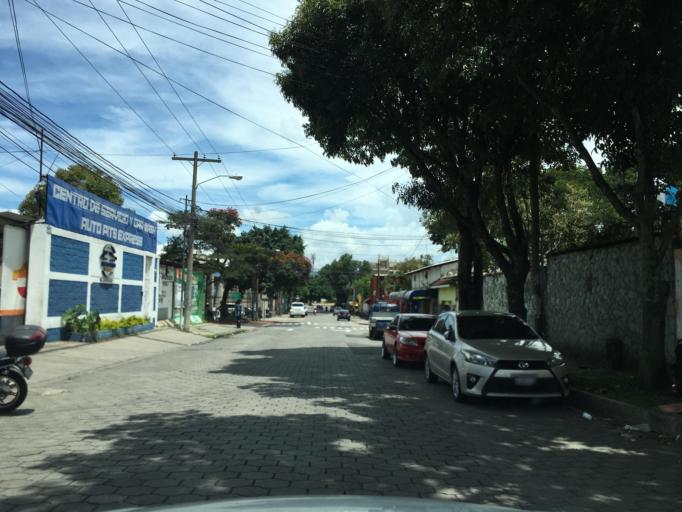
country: GT
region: Guatemala
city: Santa Catarina Pinula
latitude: 14.5871
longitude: -90.5442
